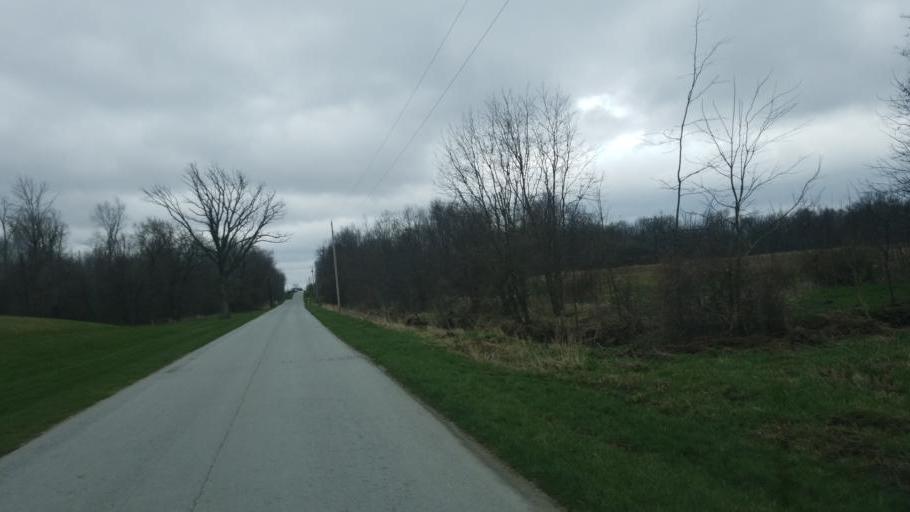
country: US
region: Ohio
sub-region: Hardin County
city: Forest
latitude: 40.6557
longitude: -83.4393
